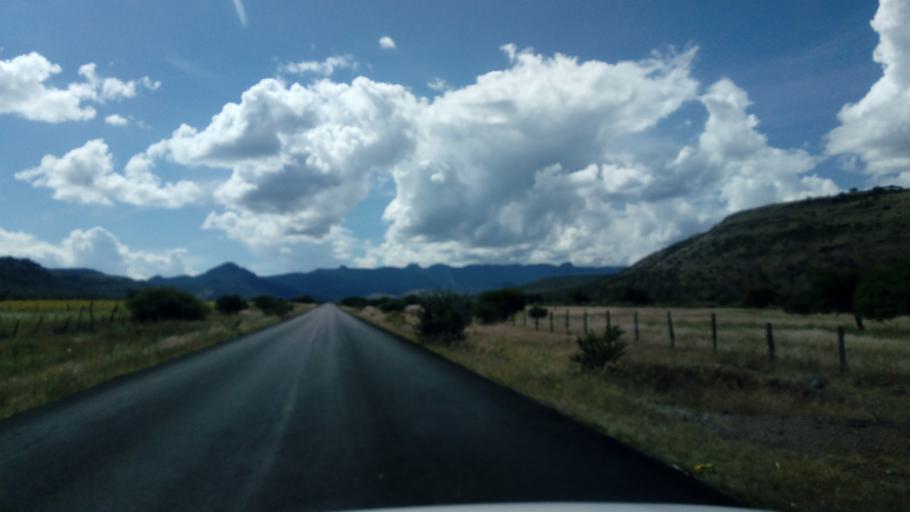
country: MX
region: Durango
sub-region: Durango
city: Jose Refugio Salcido
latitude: 23.8171
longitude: -104.4832
